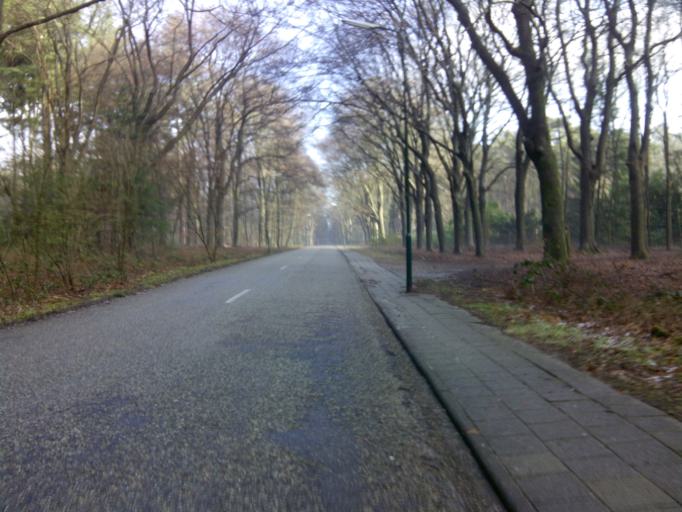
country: NL
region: Utrecht
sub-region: Gemeente Utrechtse Heuvelrug
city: Maarsbergen
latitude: 52.0287
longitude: 5.3947
